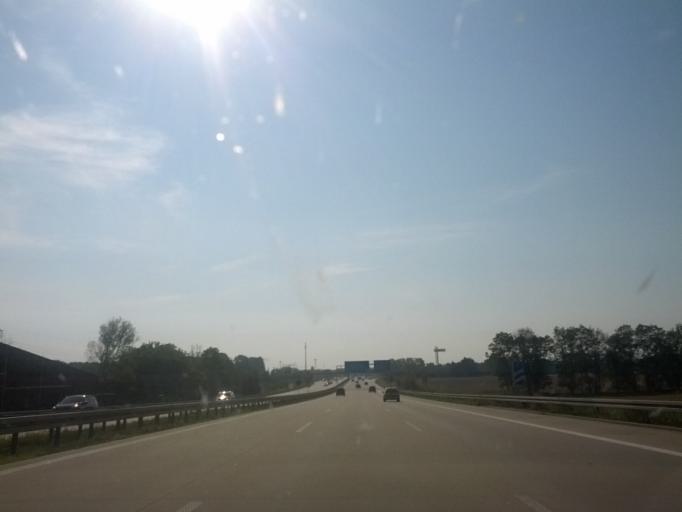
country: DE
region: Brandenburg
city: Petershagen
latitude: 52.5056
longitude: 13.7397
